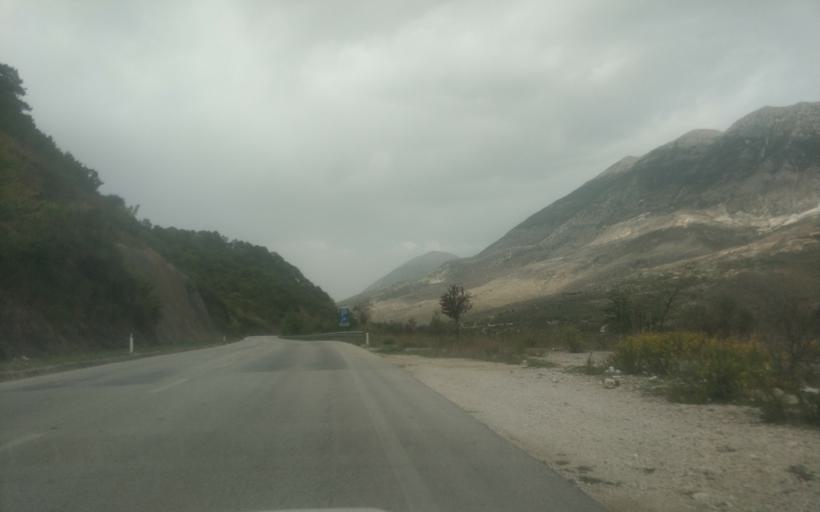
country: AL
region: Gjirokaster
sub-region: Rrethi i Gjirokastres
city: Picar
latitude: 40.2231
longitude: 20.0871
